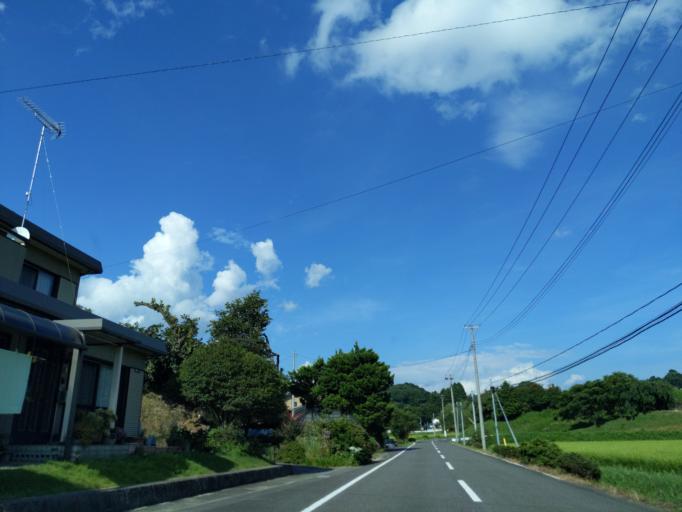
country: JP
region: Fukushima
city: Koriyama
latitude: 37.4029
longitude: 140.4251
